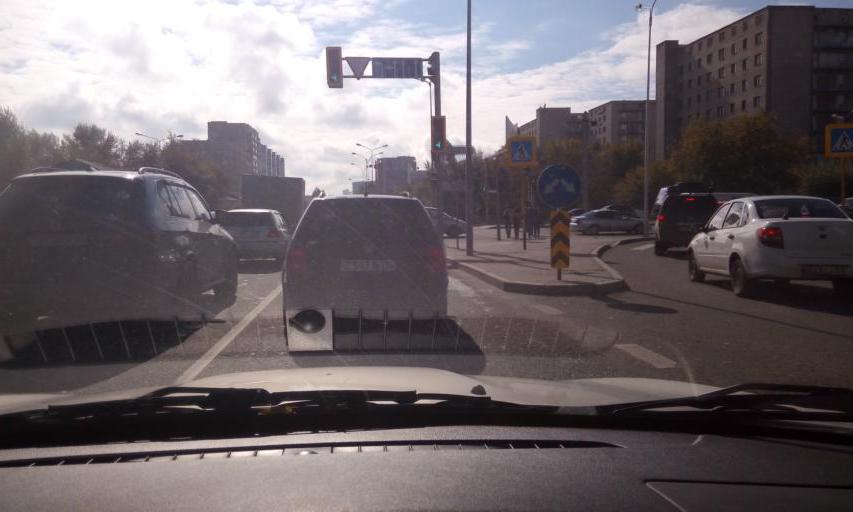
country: KZ
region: Astana Qalasy
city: Astana
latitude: 51.1762
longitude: 71.4109
